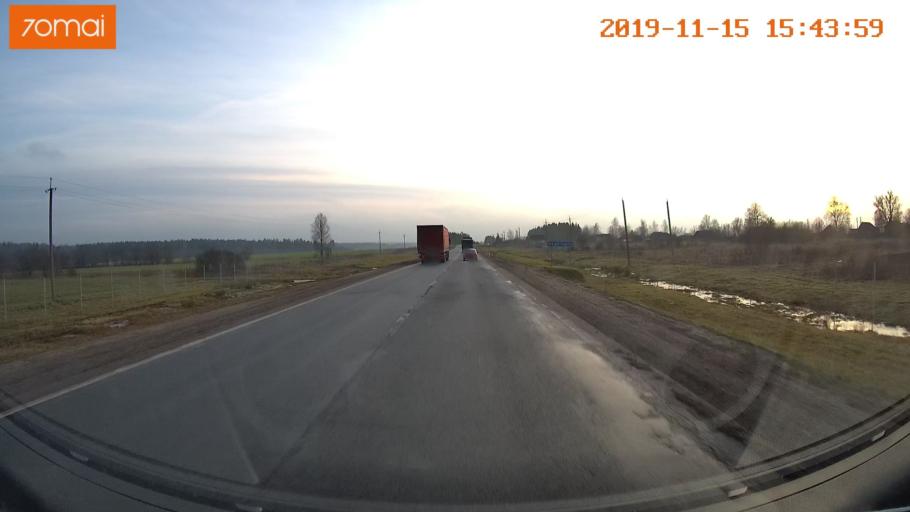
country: RU
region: Jaroslavl
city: Danilov
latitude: 57.9756
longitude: 40.0246
